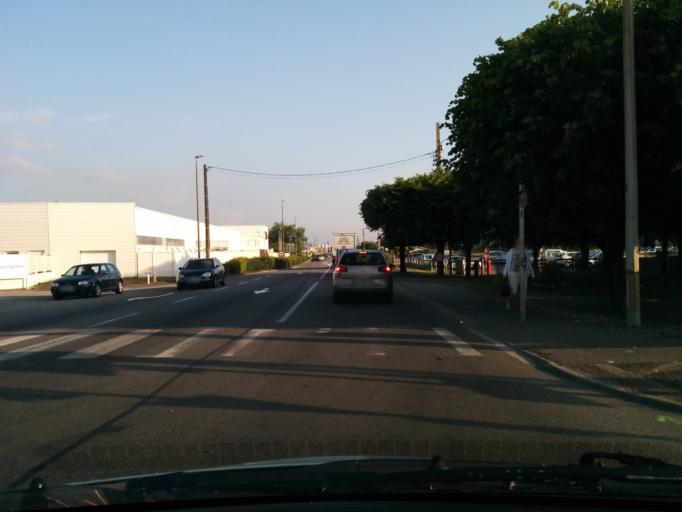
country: FR
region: Haute-Normandie
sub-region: Departement de l'Eure
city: Saint-Marcel
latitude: 49.1058
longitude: 1.4576
